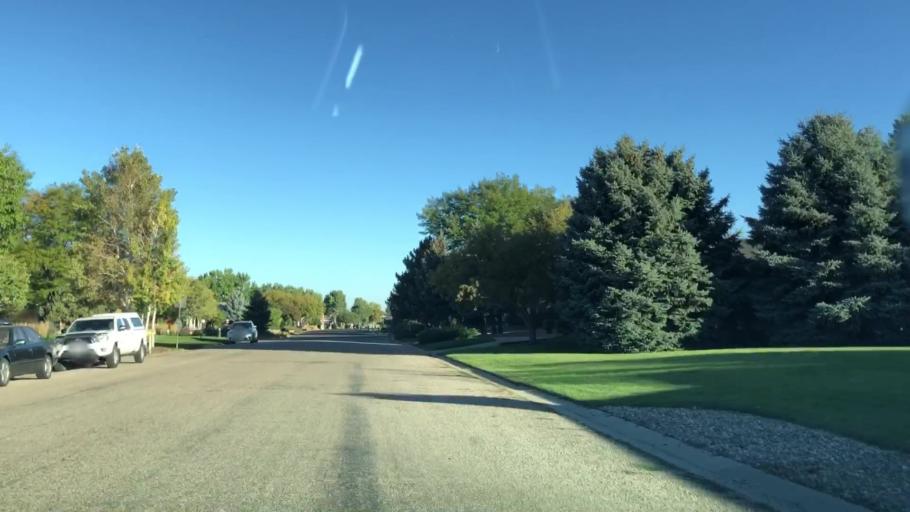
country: US
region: Colorado
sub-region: Larimer County
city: Loveland
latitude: 40.4300
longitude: -105.0225
